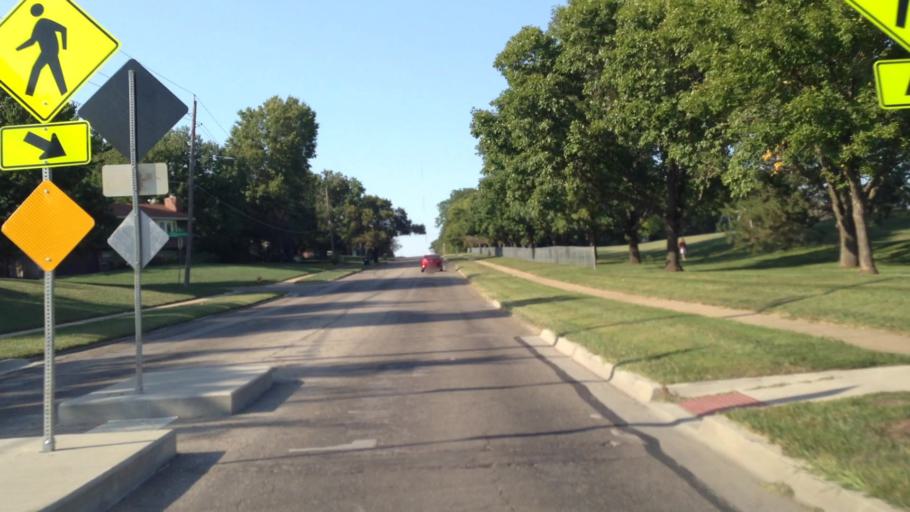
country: US
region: Kansas
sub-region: Douglas County
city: Lawrence
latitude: 38.9367
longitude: -95.2698
